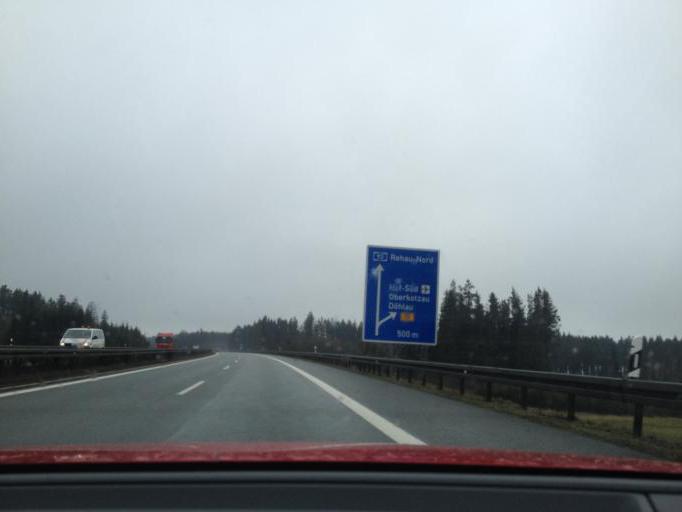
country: DE
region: Bavaria
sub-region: Upper Franconia
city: Rehau
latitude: 50.2750
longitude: 12.0244
